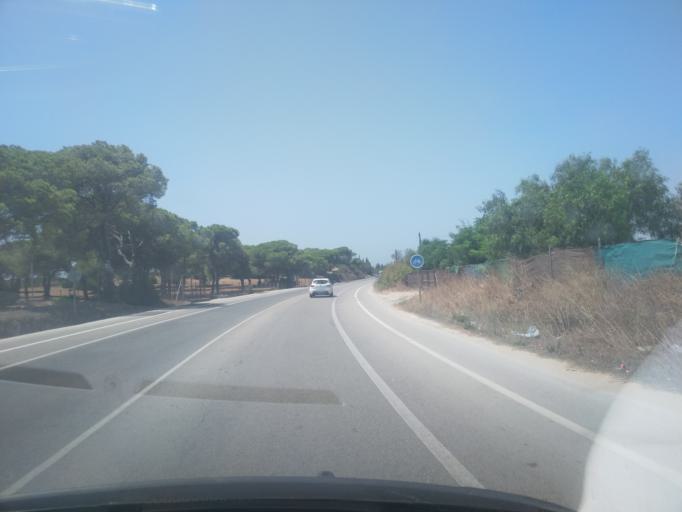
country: ES
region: Andalusia
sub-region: Provincia de Cadiz
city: Chiclana de la Frontera
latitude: 36.3888
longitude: -6.1389
